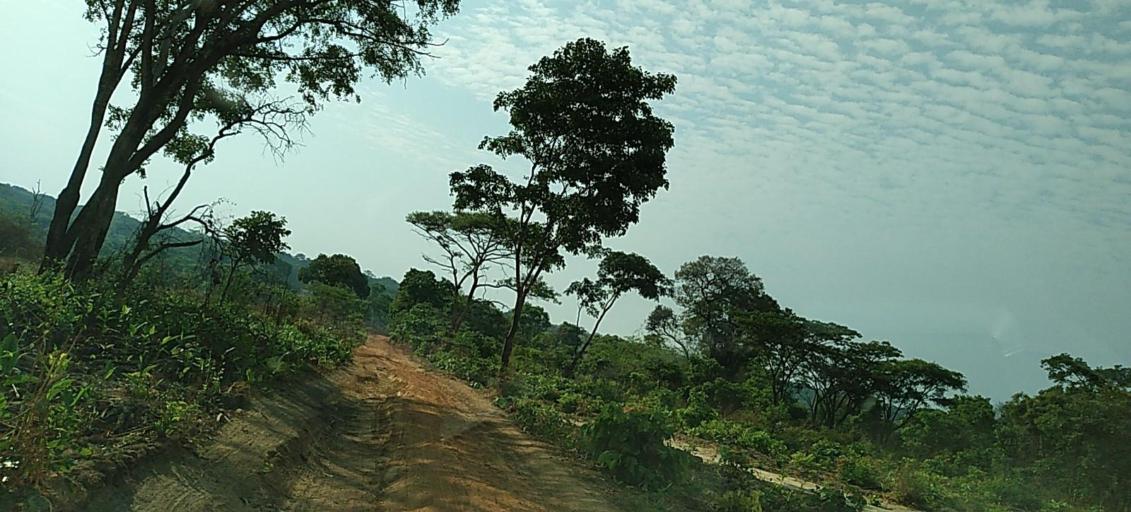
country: ZM
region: Copperbelt
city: Kalulushi
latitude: -13.0054
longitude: 27.7166
